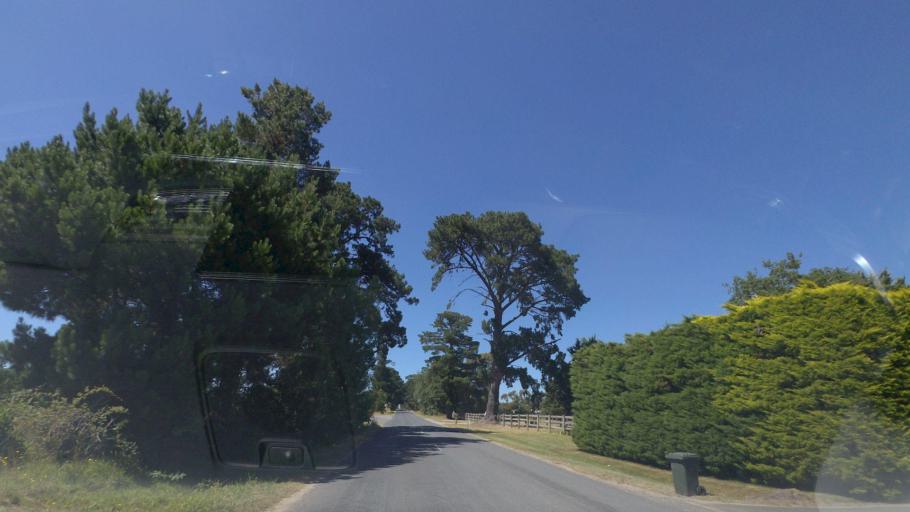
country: AU
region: Victoria
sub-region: Mornington Peninsula
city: Moorooduc
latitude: -38.2559
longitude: 145.1272
